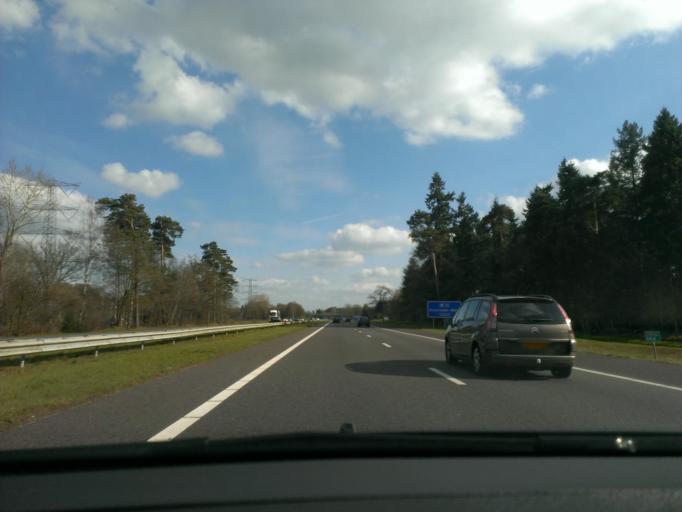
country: NL
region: Overijssel
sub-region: Gemeente Hengelo
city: Hengelo
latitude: 52.2200
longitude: 6.7975
